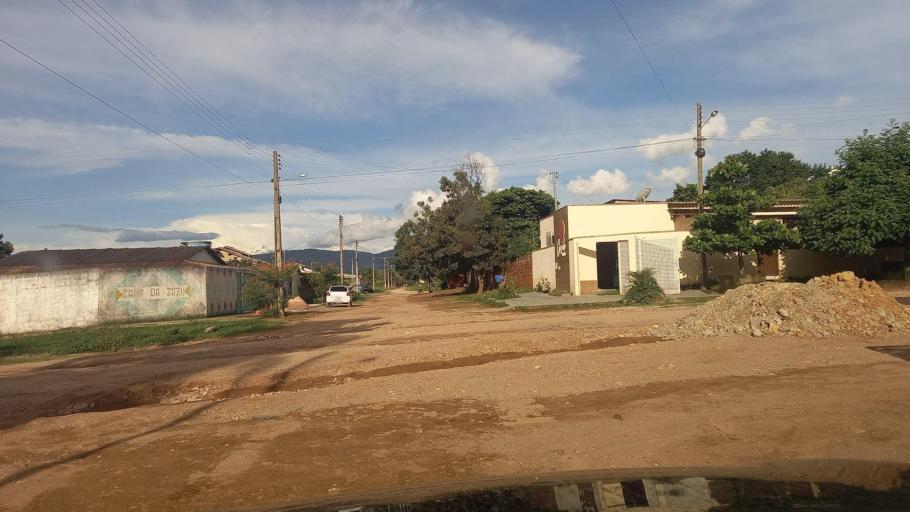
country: BR
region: Goias
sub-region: Cavalcante
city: Cavalcante
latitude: -13.7934
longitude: -47.4417
